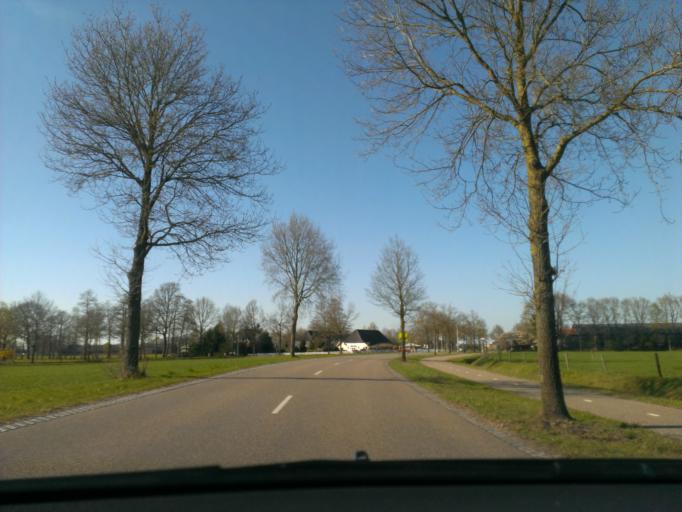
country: NL
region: Overijssel
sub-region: Gemeente Twenterand
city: Den Ham
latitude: 52.4256
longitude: 6.4798
